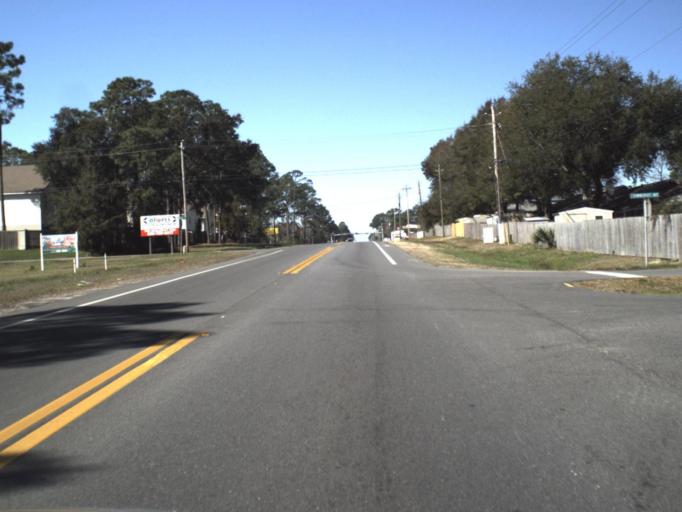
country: US
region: Florida
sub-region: Bay County
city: Callaway
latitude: 30.1529
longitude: -85.5609
